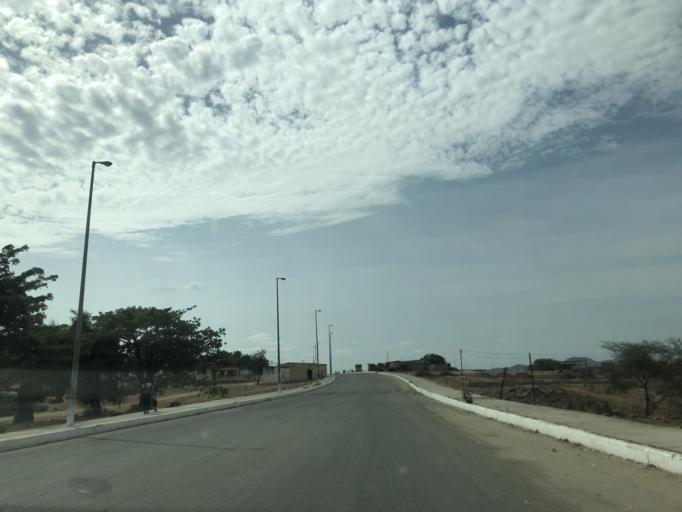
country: AO
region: Benguela
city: Benguela
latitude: -13.0310
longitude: 13.7380
